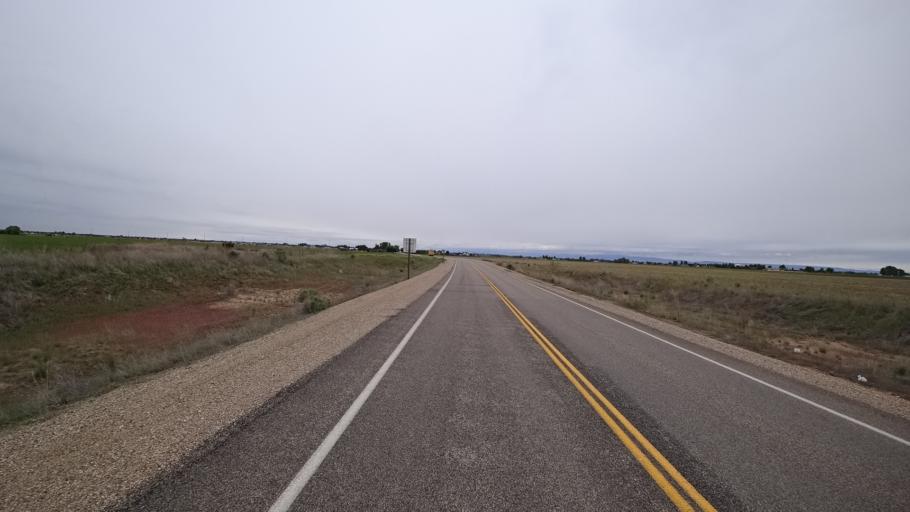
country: US
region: Idaho
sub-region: Ada County
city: Star
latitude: 43.6614
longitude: -116.4729
